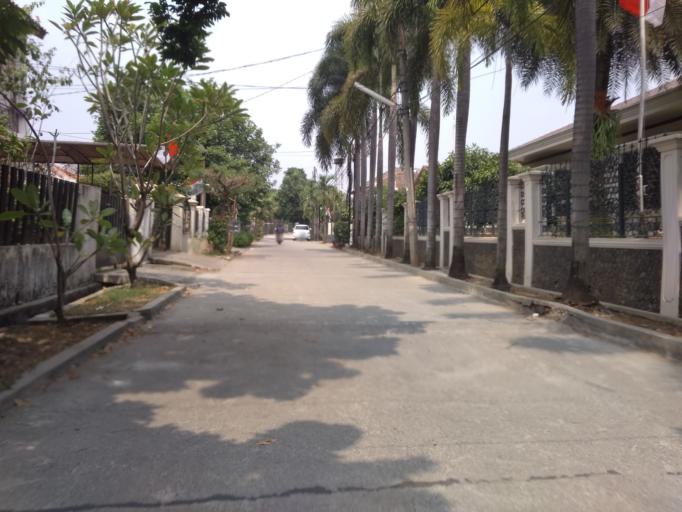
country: ID
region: West Java
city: Pamulang
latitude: -6.3203
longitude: 106.7907
